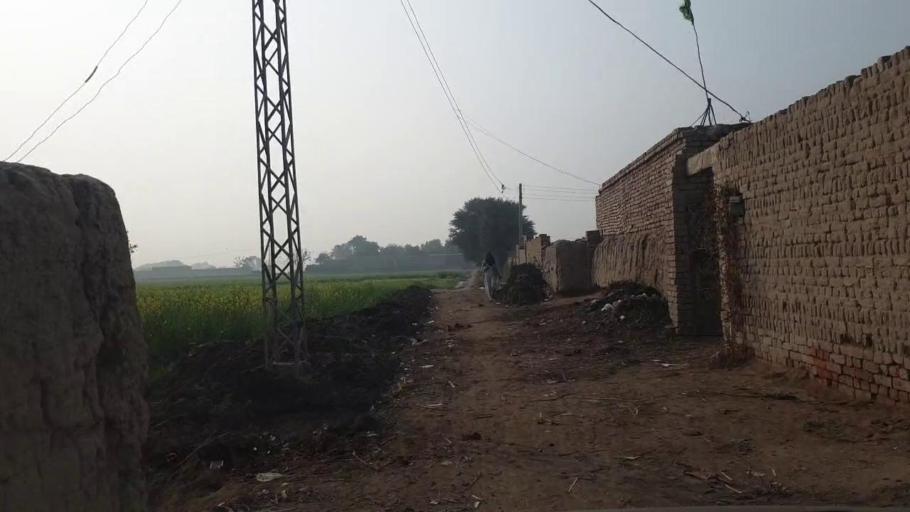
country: PK
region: Sindh
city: Hala
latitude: 25.8715
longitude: 68.3932
